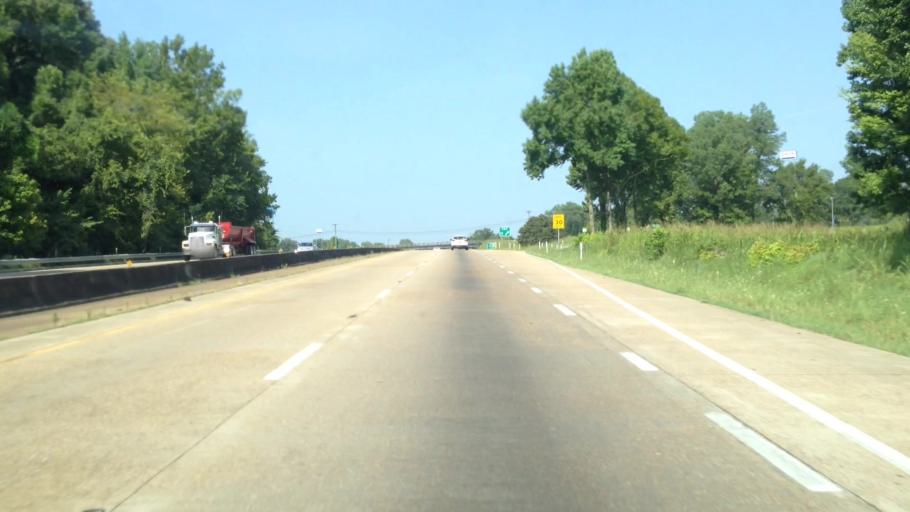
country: US
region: Mississippi
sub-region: Warren County
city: Beechwood
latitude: 32.3560
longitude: -90.7299
